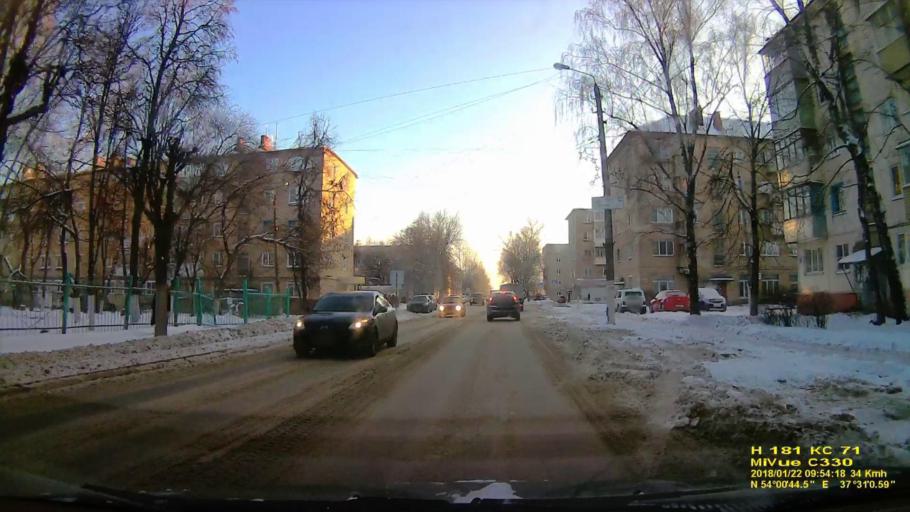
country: RU
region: Tula
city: Shchekino
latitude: 54.0126
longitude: 37.5170
